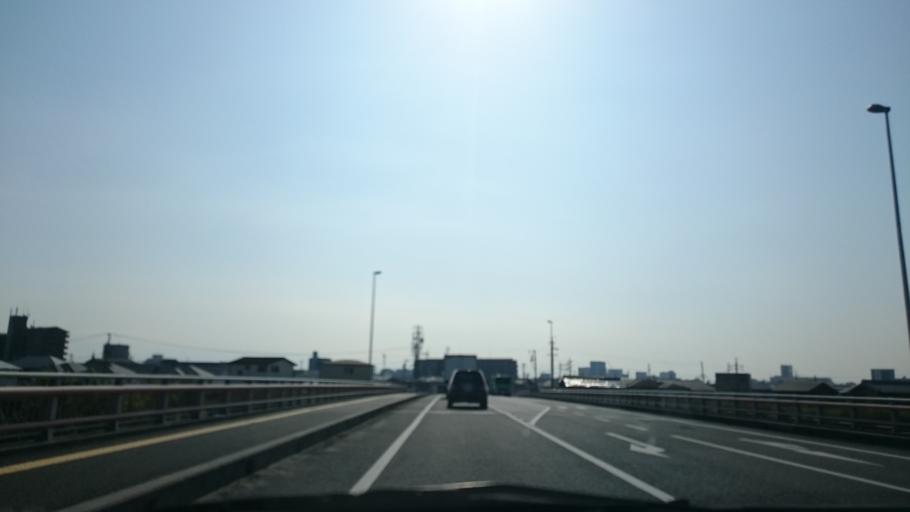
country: JP
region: Mie
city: Yokkaichi
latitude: 34.9808
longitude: 136.6211
